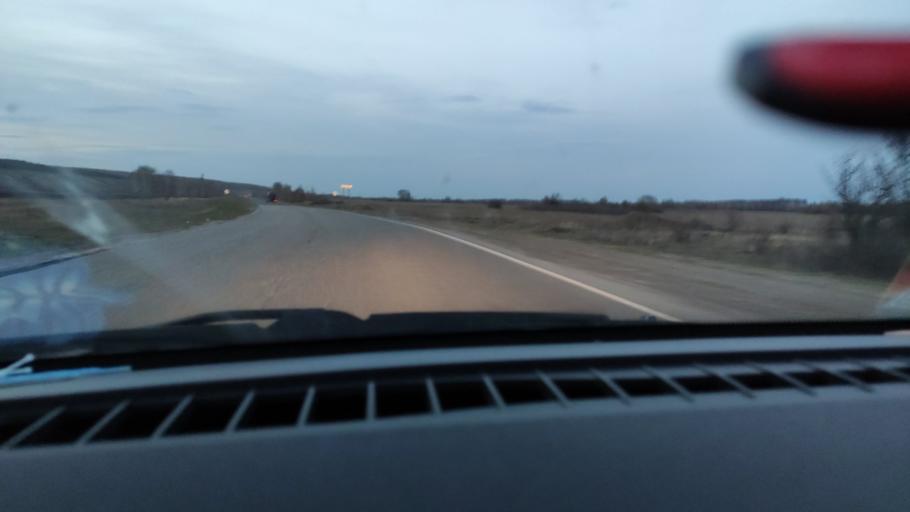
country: RU
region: Saratov
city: Sinodskoye
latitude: 52.0545
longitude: 46.7565
